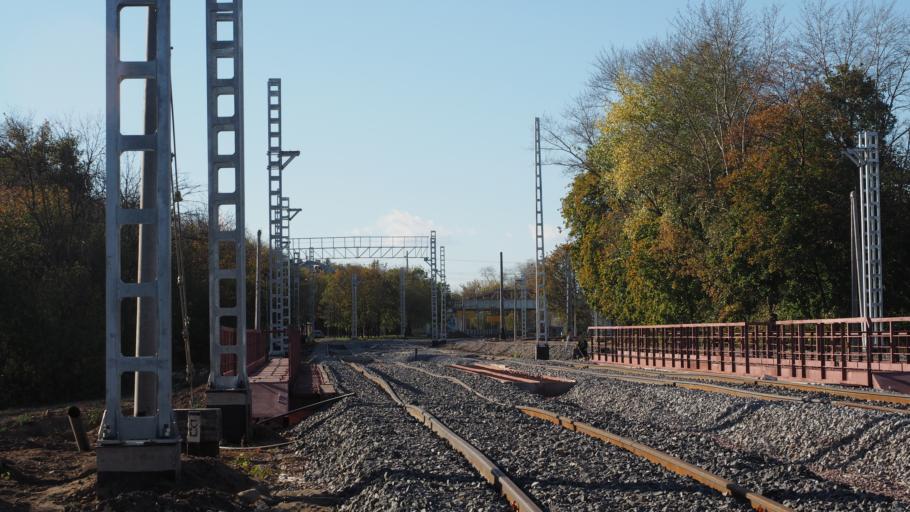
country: RU
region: Moscow
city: Novovladykino
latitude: 55.8477
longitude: 37.5811
